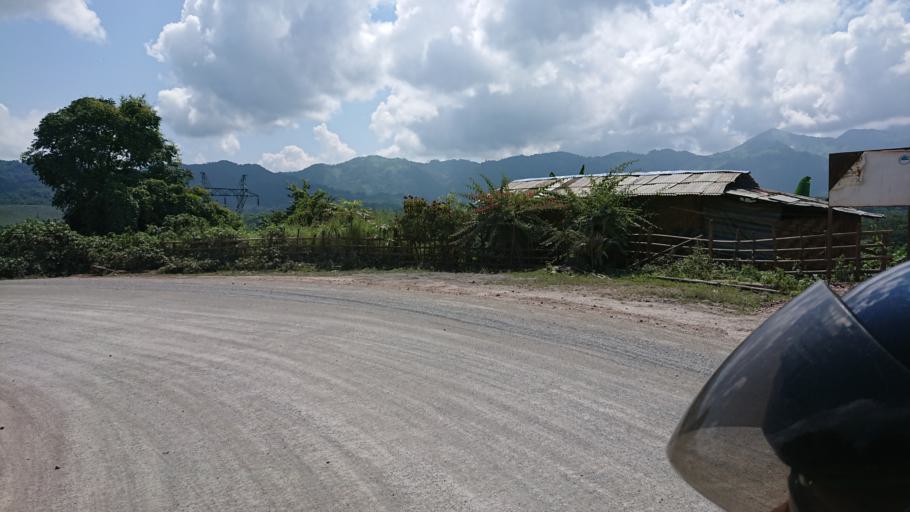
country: MM
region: Shan
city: Taunggyi
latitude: 20.8116
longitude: 97.3231
